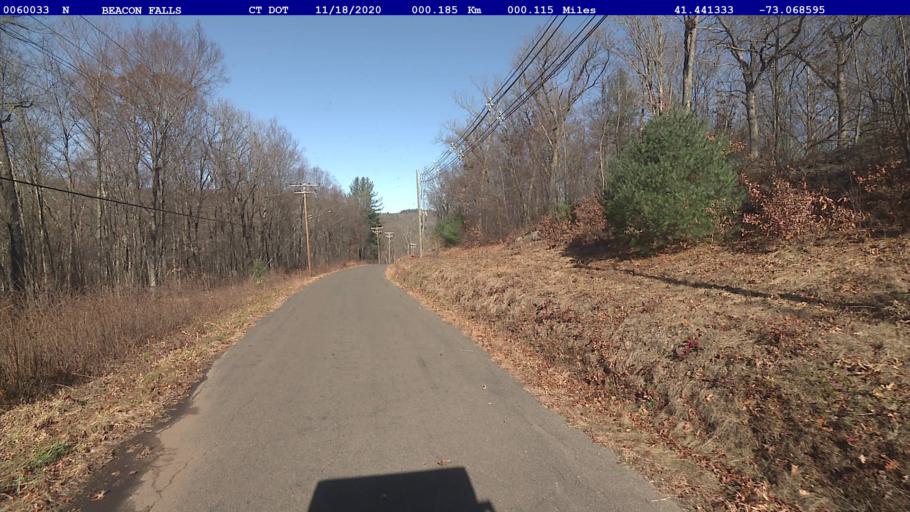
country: US
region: Connecticut
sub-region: New Haven County
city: Seymour
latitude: 41.4413
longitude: -73.0686
